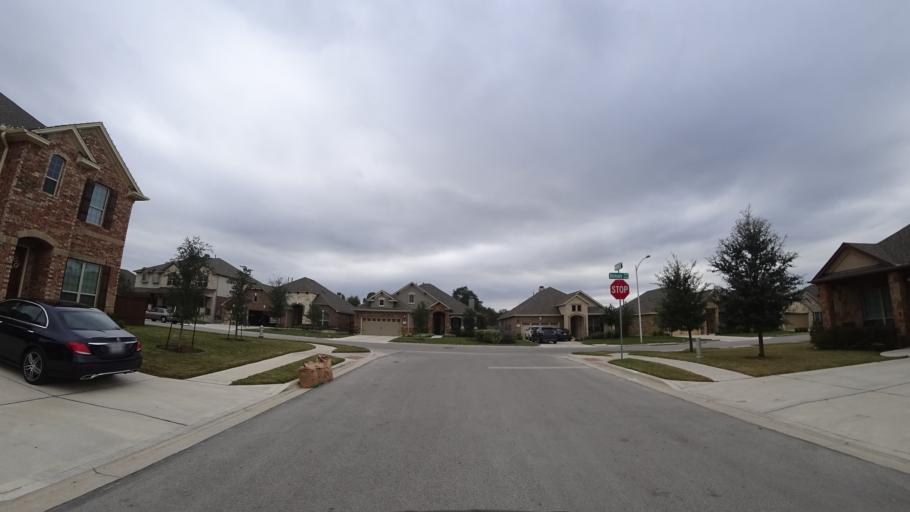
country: US
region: Texas
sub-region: Travis County
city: Manchaca
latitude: 30.1420
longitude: -97.8517
